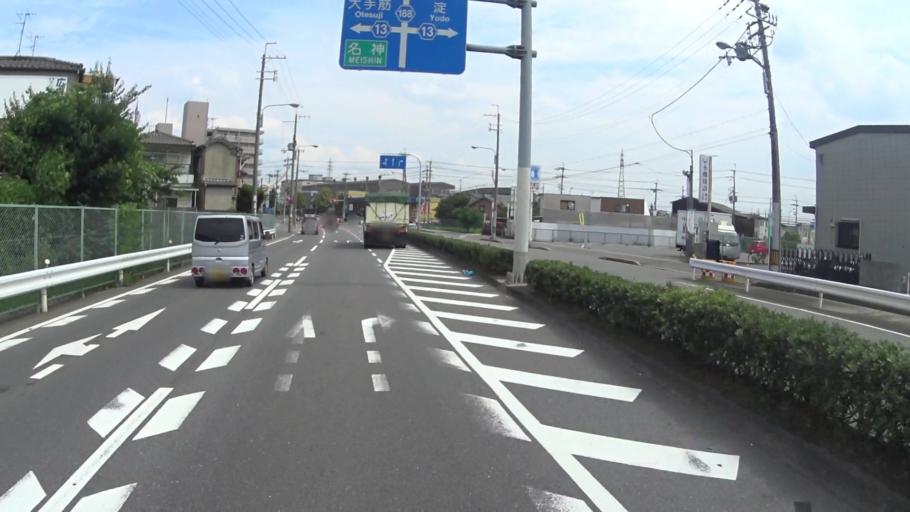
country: JP
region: Kyoto
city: Muko
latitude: 34.9276
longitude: 135.7378
